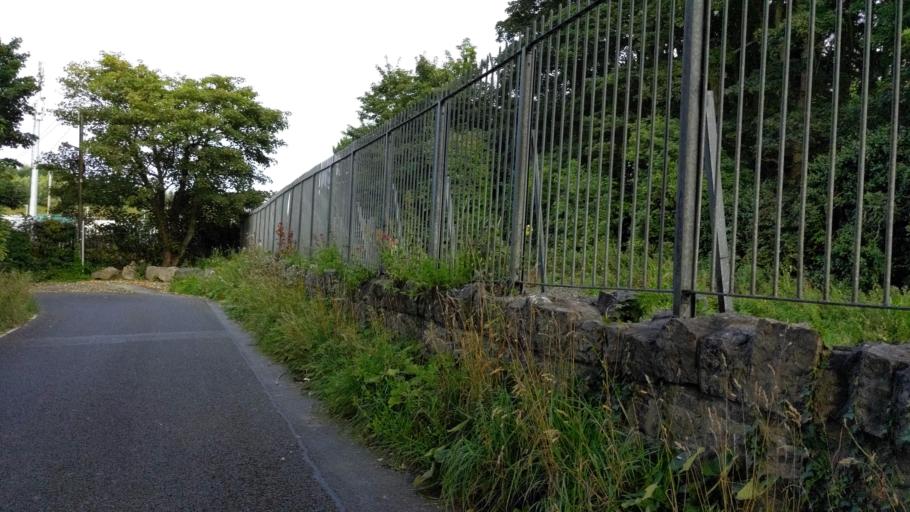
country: IE
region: Leinster
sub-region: Lu
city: Drogheda
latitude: 53.7110
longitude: -6.3366
